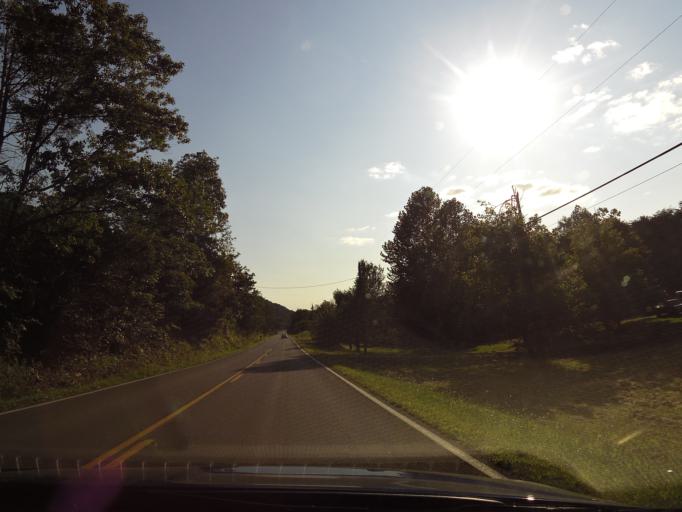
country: US
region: Tennessee
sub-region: Union County
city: Condon
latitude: 36.1971
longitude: -83.8078
